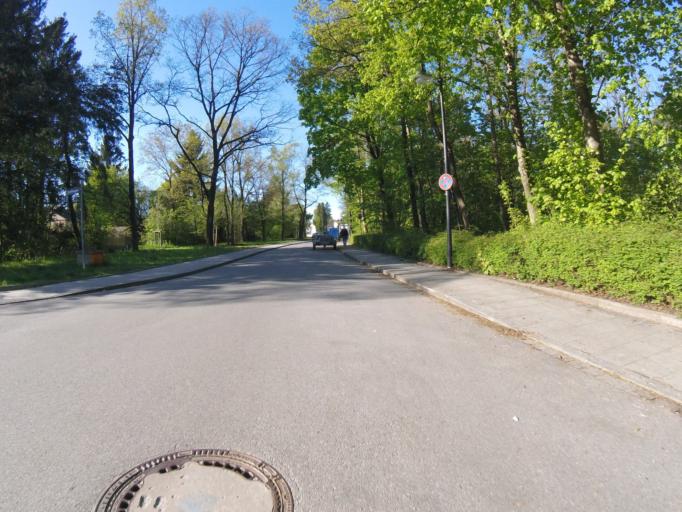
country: DE
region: Bavaria
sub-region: Upper Bavaria
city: Ottobrunn
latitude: 48.0588
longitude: 11.6615
